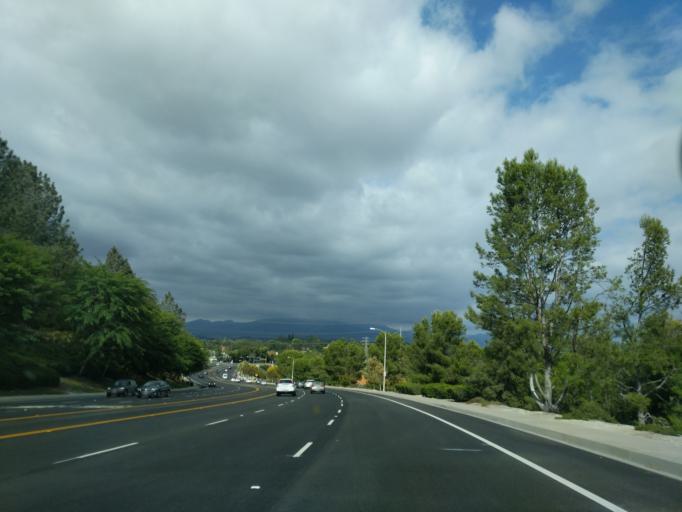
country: US
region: California
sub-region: Orange County
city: Laguna Woods
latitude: 33.5881
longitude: -117.7164
